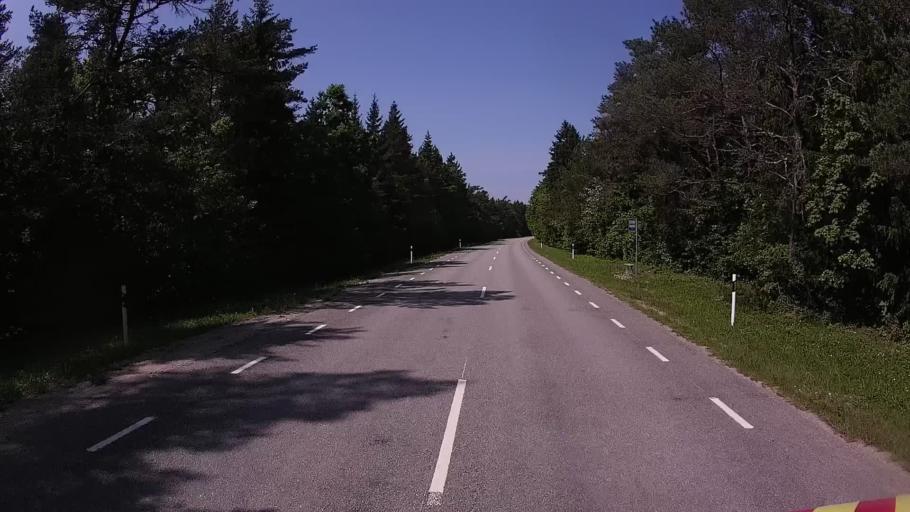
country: EE
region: Saare
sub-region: Kuressaare linn
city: Kuressaare
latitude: 58.3536
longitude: 22.0723
